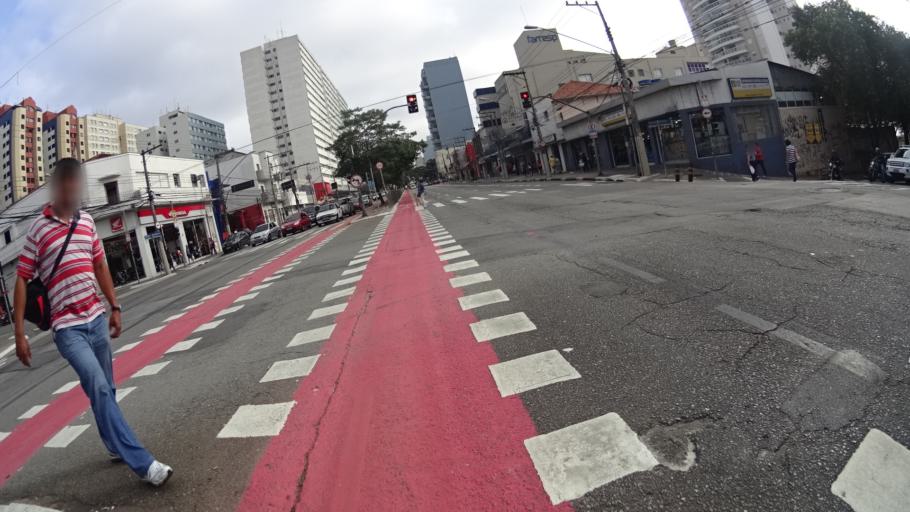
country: BR
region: Sao Paulo
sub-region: Sao Paulo
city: Sao Paulo
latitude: -23.6152
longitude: -46.6386
